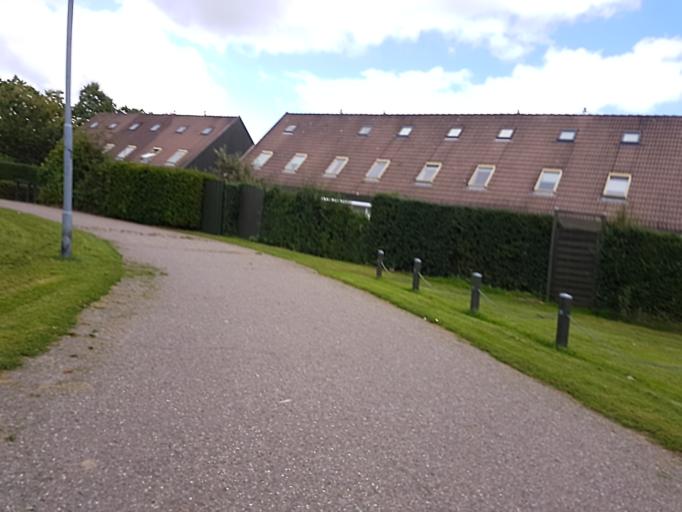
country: DK
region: Zealand
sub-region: Roskilde Kommune
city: Jyllinge
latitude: 55.7500
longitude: 12.1118
